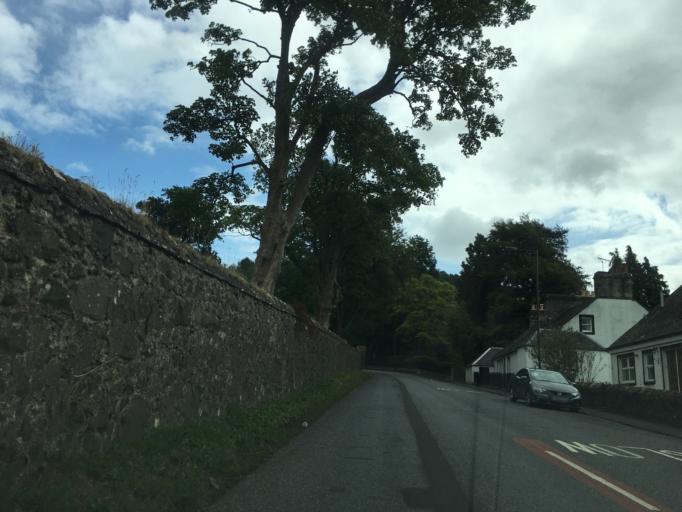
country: GB
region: Scotland
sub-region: Stirling
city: Stirling
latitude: 56.1405
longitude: -3.9232
